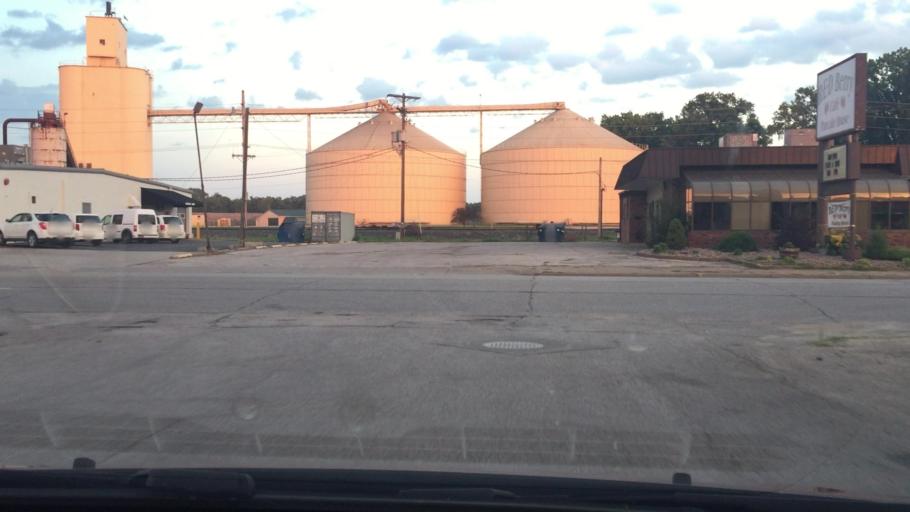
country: US
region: Iowa
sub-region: Muscatine County
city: Muscatine
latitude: 41.4097
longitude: -91.0631
